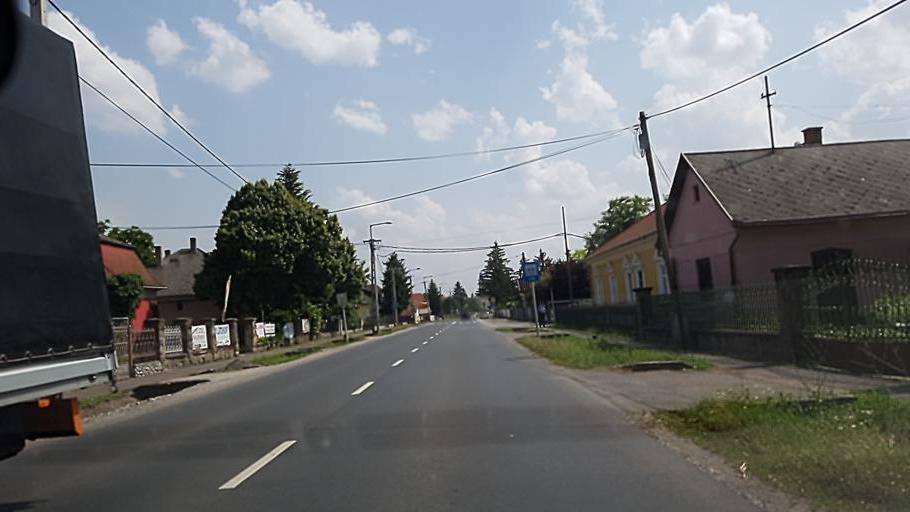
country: HU
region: Heves
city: Besenyotelek
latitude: 47.7046
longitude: 20.4272
